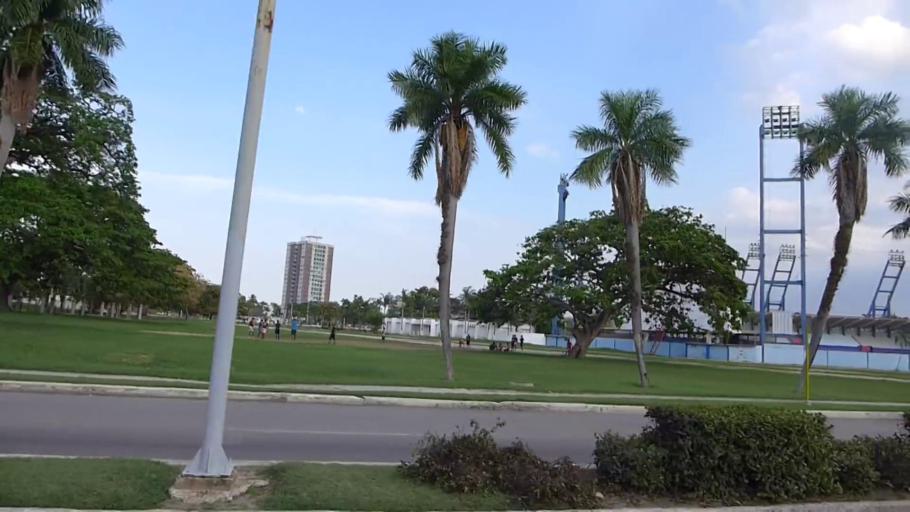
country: CU
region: Camaguey
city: Camaguey
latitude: 21.3801
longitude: -77.9115
